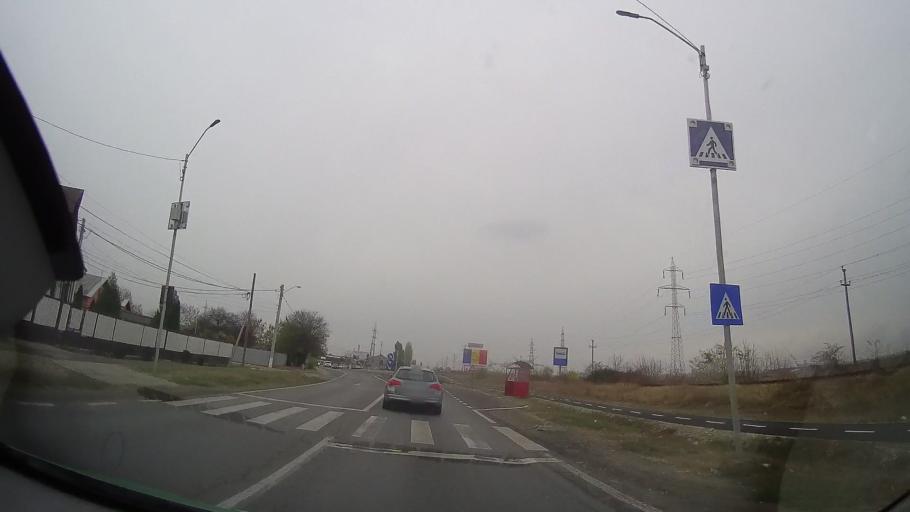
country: RO
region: Prahova
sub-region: Comuna Blejoiu
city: Ploiestiori
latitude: 44.9765
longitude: 26.0174
